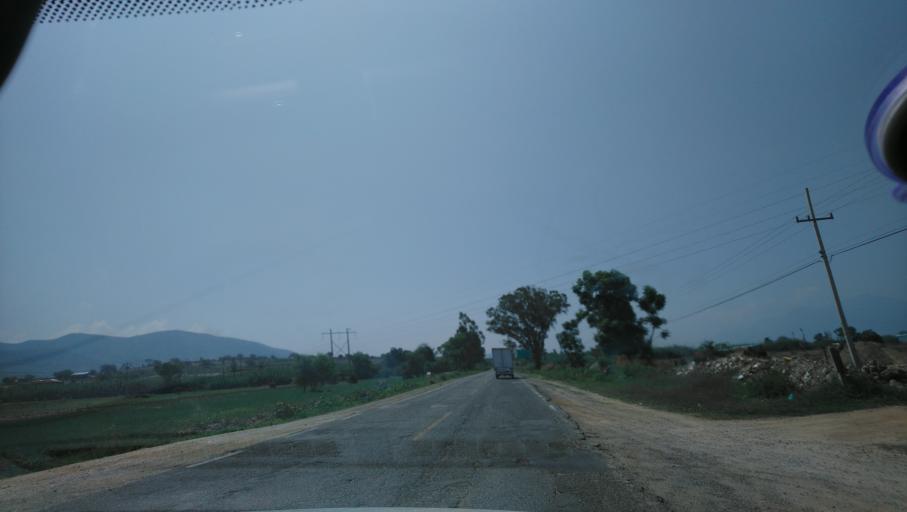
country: MX
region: Oaxaca
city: Santa Maria del Tule
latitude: 17.0407
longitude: -96.6237
